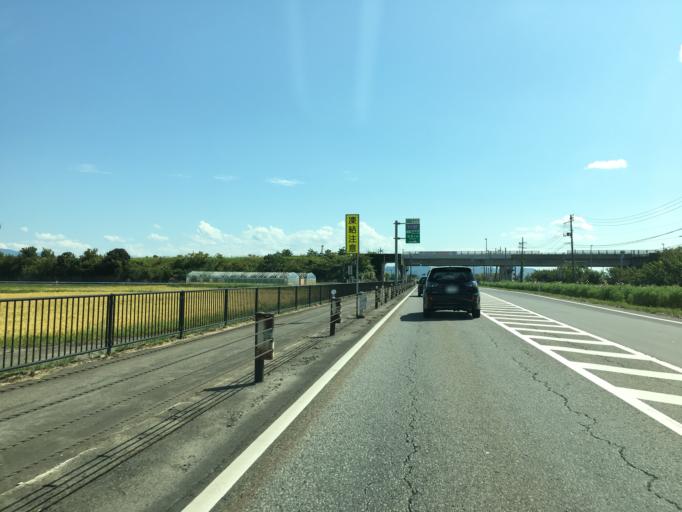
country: JP
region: Niigata
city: Niitsu-honcho
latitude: 37.8224
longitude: 139.0988
